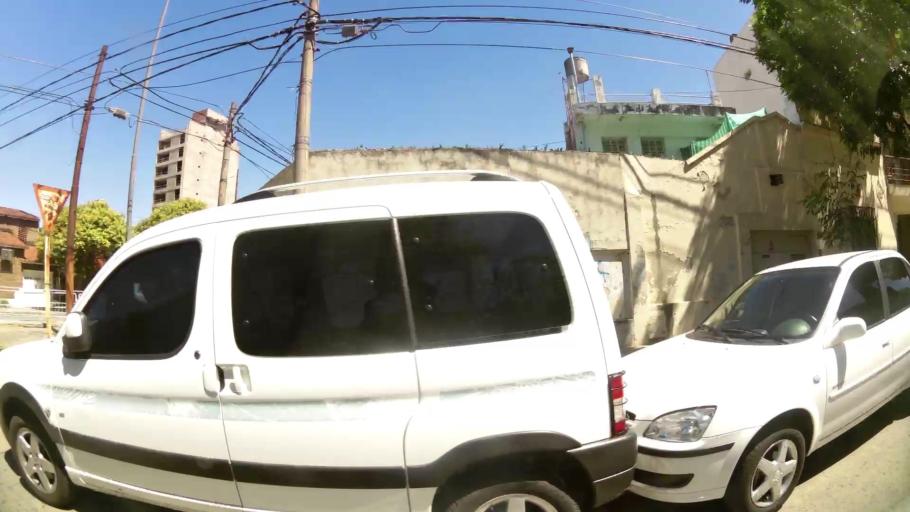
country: AR
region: Santa Fe
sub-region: Departamento de Rosario
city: Rosario
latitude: -32.9335
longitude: -60.6722
